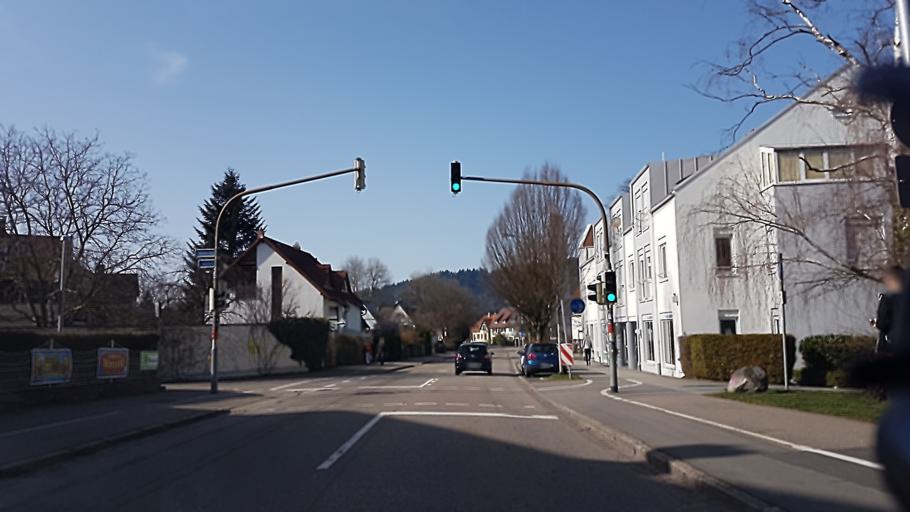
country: DE
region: Baden-Wuerttemberg
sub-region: Freiburg Region
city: Freiburg
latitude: 47.9823
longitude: 7.8987
